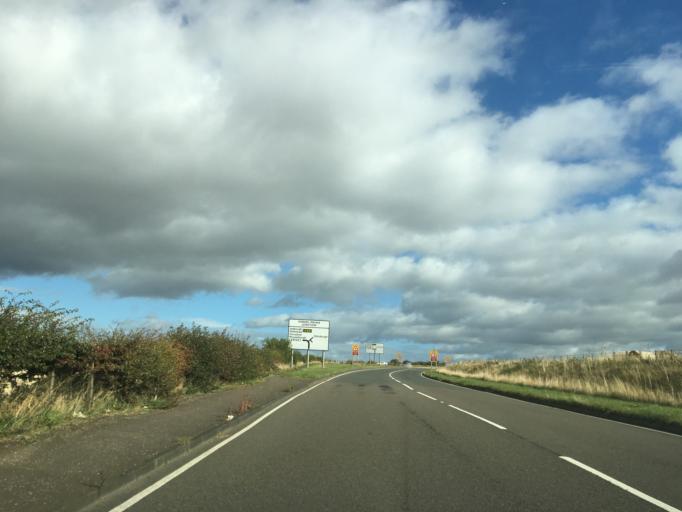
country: GB
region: Scotland
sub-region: Fife
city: Pathhead
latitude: 55.8911
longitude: -3.0102
